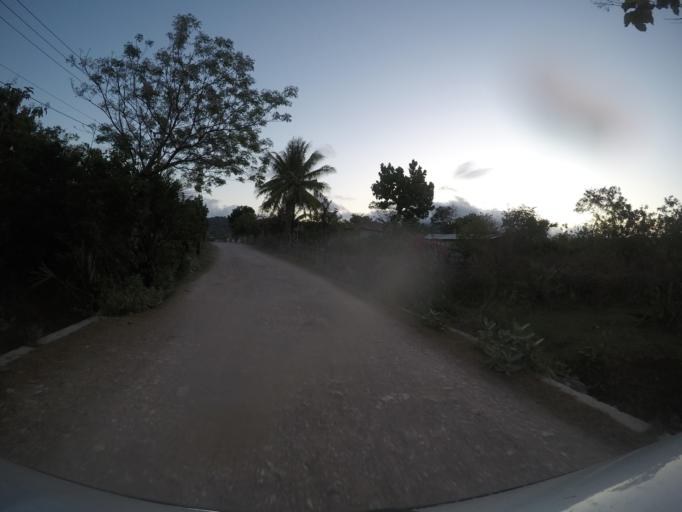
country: TL
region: Viqueque
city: Viqueque
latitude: -8.7723
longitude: 126.6398
